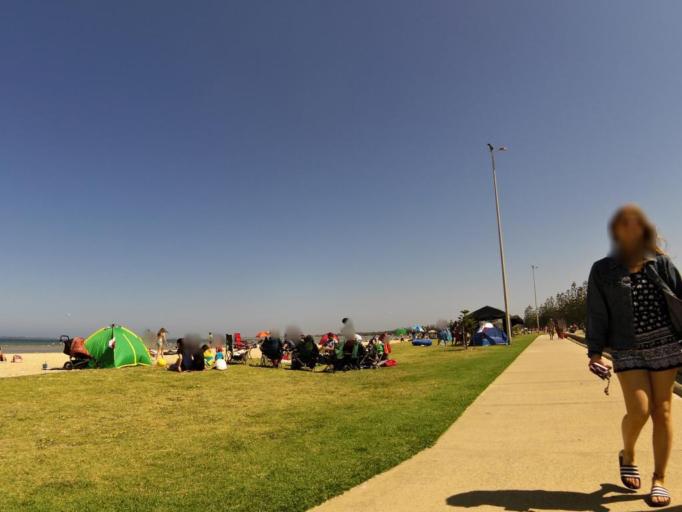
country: AU
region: Victoria
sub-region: Hobsons Bay
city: Altona
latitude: -37.8707
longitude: 144.8282
